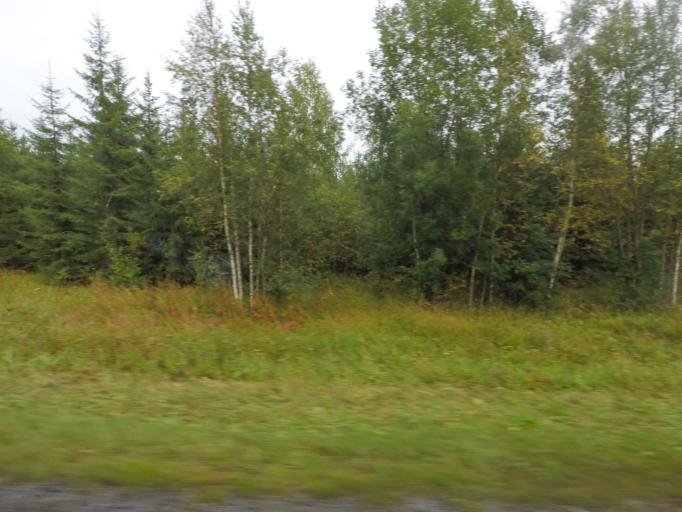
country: FI
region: Southern Savonia
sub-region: Pieksaemaeki
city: Joroinen
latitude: 62.0533
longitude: 27.8042
